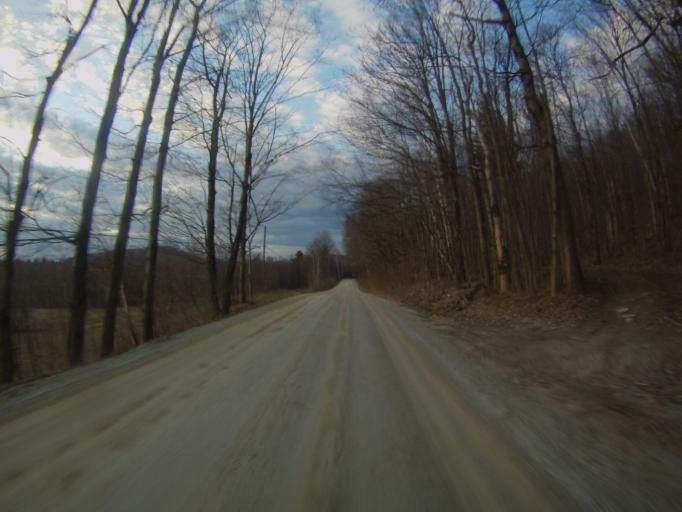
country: US
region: Vermont
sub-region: Rutland County
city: Brandon
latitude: 43.8804
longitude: -73.0124
